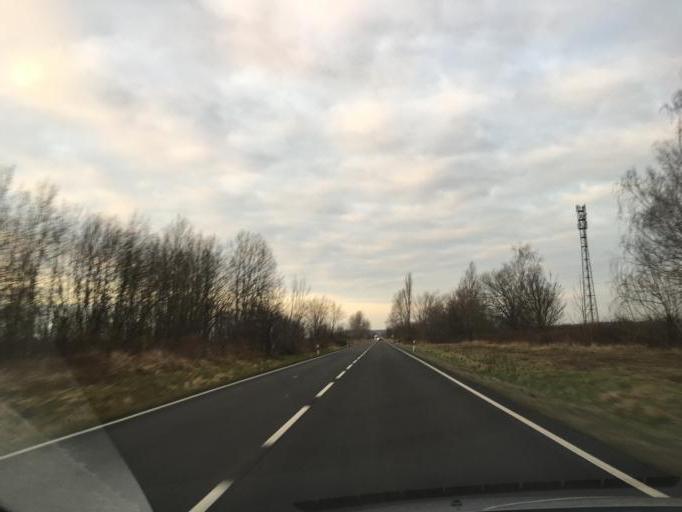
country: DE
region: Saxony
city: Espenhain
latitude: 51.2049
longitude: 12.4544
